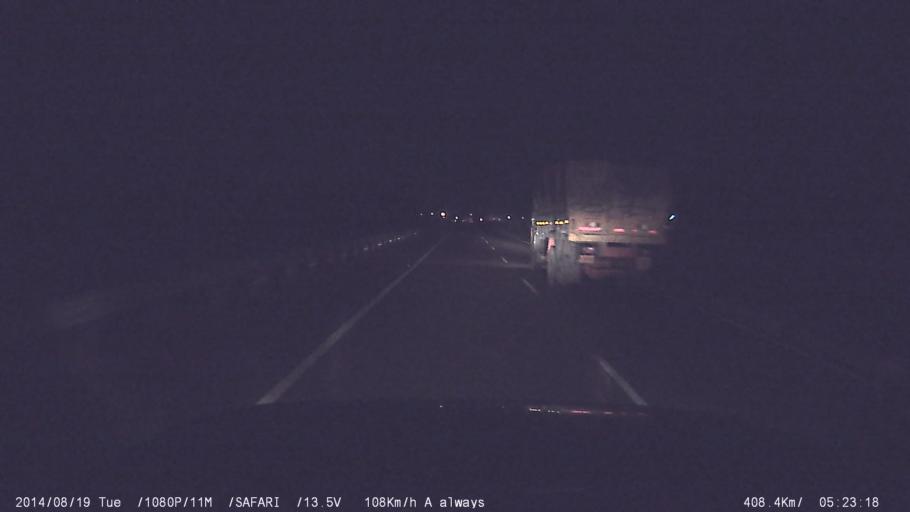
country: IN
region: Tamil Nadu
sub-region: Salem
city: Ilampillai
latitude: 11.5587
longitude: 78.0141
